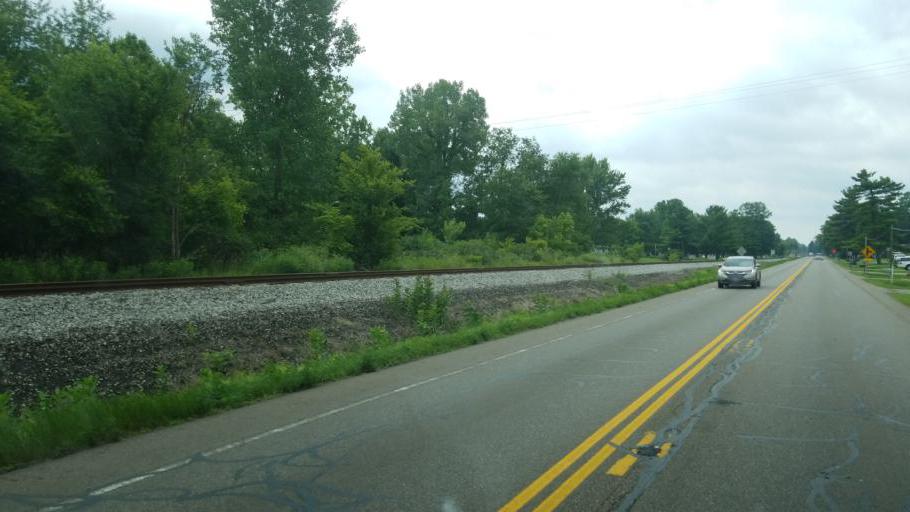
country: US
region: Ohio
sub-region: Licking County
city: Newark
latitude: 40.1391
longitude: -82.4273
